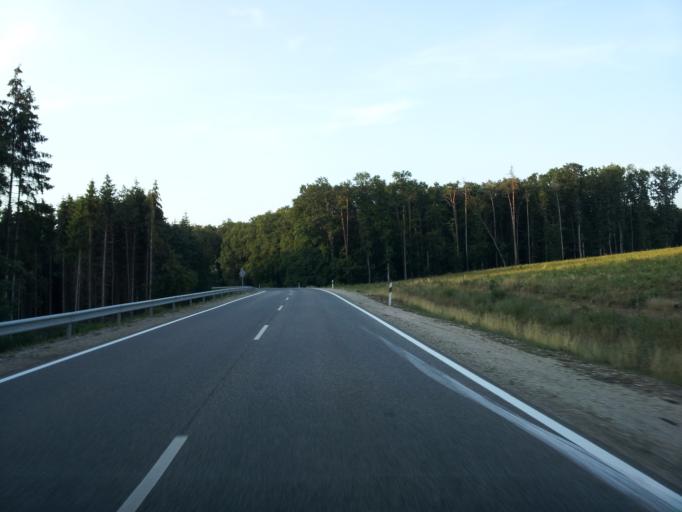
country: HU
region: Zala
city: Zalalovo
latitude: 46.7849
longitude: 16.5671
